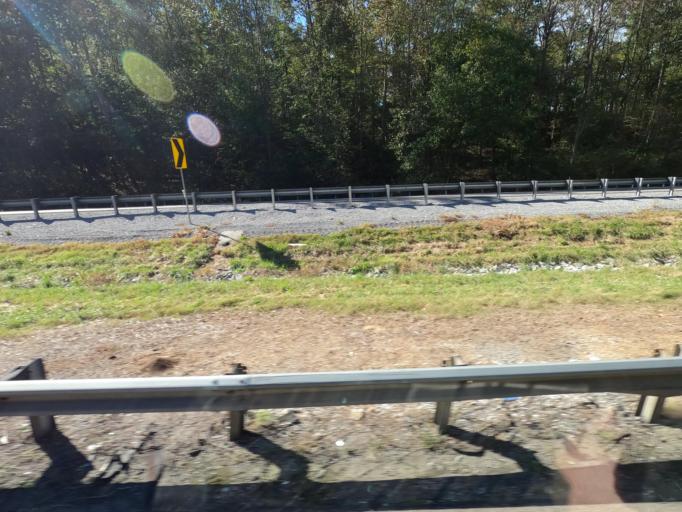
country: US
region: Tennessee
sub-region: Dickson County
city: White Bluff
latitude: 36.0300
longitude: -87.2055
